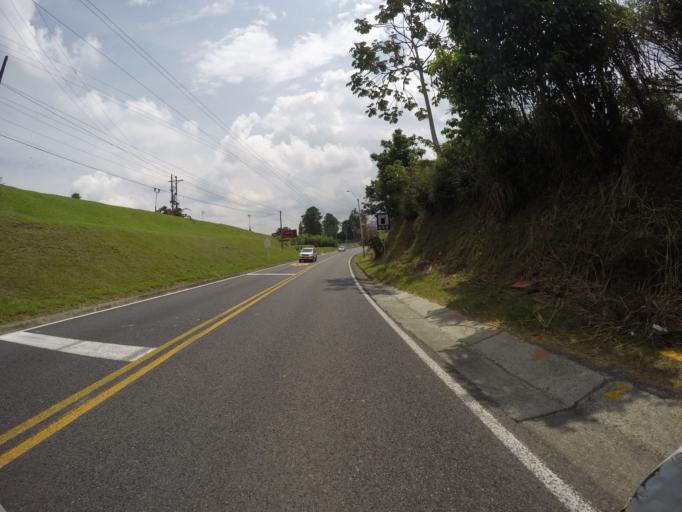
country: CO
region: Risaralda
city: Pereira
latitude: 4.7710
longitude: -75.6913
